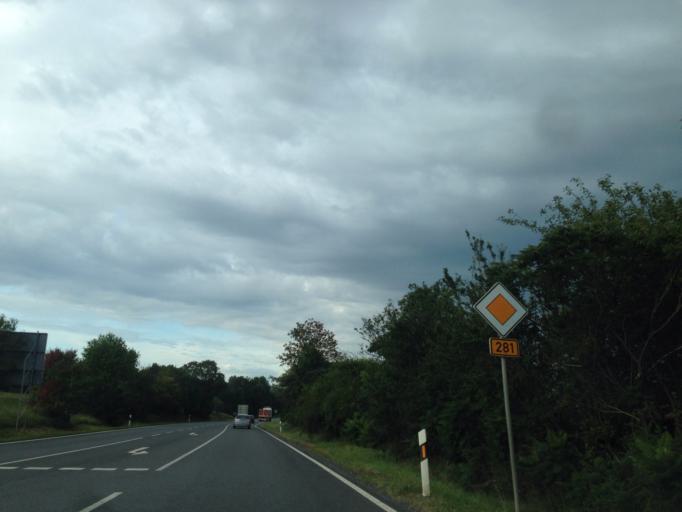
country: DE
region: Thuringia
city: Oppurg
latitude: 50.7110
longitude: 11.6583
